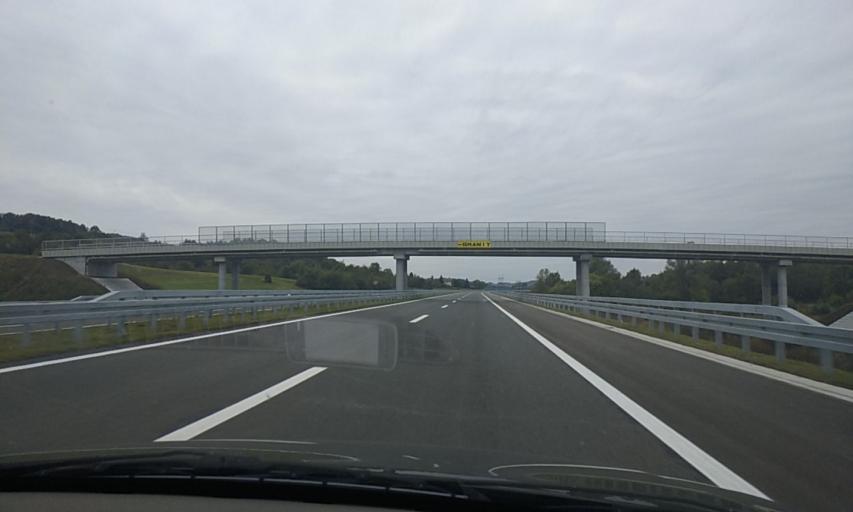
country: BA
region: Republika Srpska
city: Prnjavor
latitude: 44.8919
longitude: 17.5849
